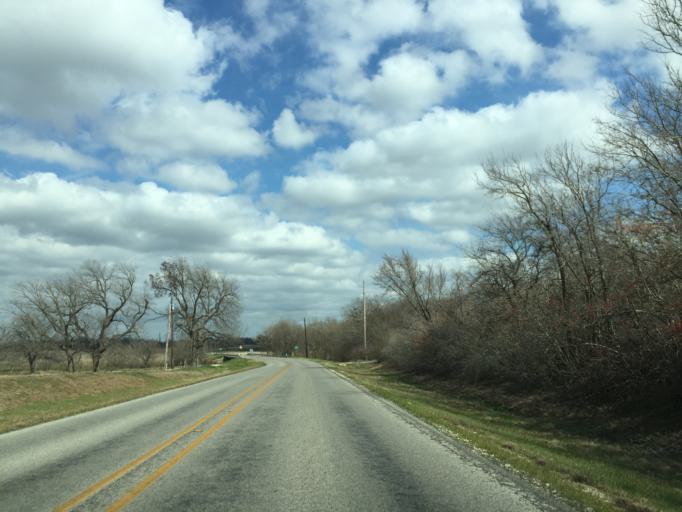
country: US
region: Texas
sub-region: Williamson County
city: Granger
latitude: 30.7061
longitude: -97.4681
